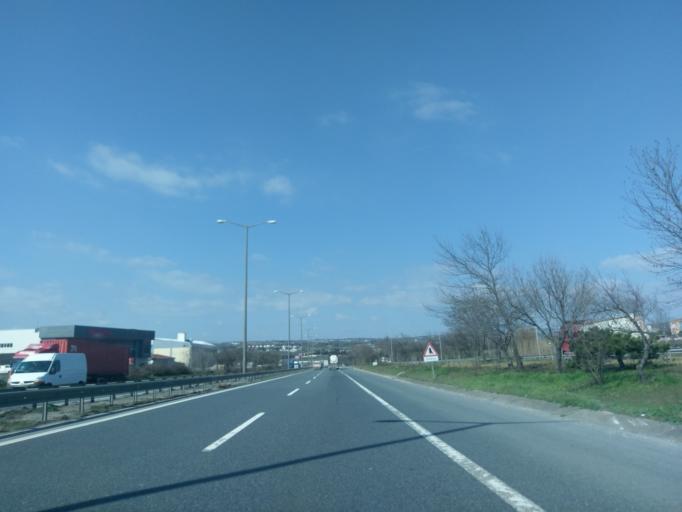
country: TR
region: Istanbul
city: Ortakoy
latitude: 41.0857
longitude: 28.3680
